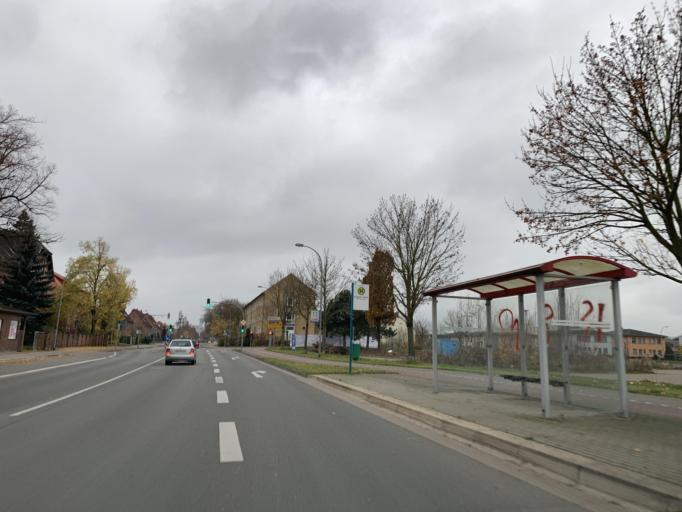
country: DE
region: Mecklenburg-Vorpommern
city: Neubrandenburg
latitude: 53.5706
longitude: 13.2781
